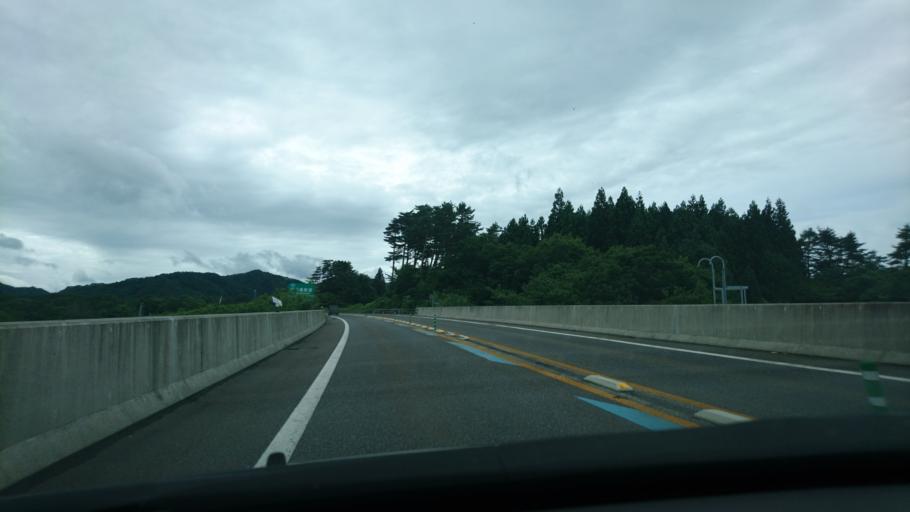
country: JP
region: Iwate
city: Miyako
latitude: 39.8760
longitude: 141.9341
